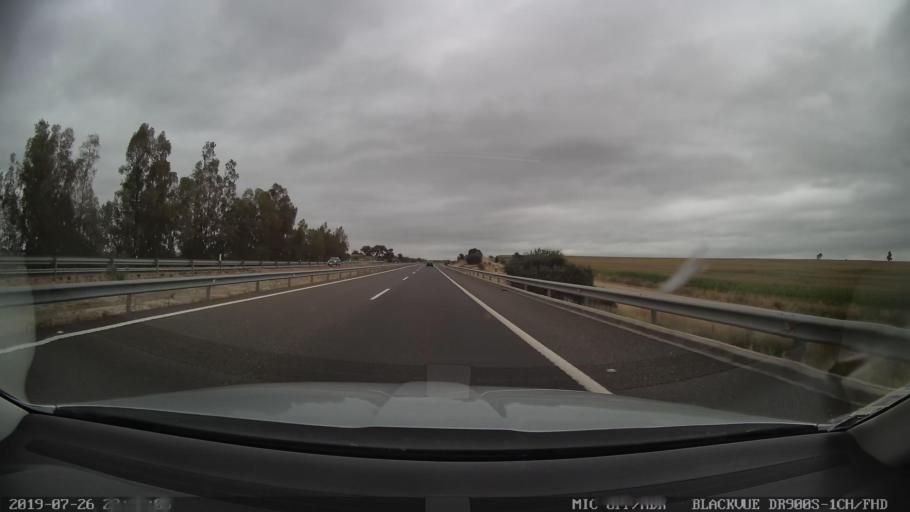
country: ES
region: Extremadura
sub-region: Provincia de Badajoz
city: Santa Amalia
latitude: 39.0141
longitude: -6.0868
